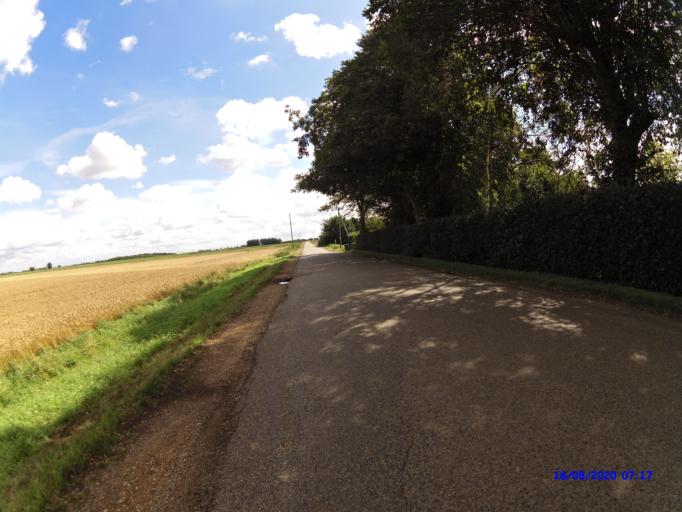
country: GB
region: England
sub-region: Cambridgeshire
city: Whittlesey
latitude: 52.5341
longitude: -0.1051
